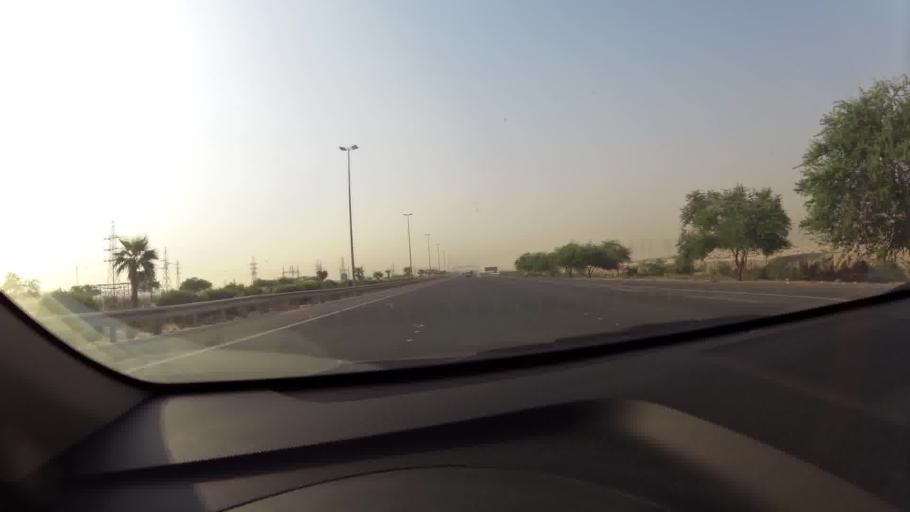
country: KW
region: Al Ahmadi
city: Al Fahahil
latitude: 28.8996
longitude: 48.2192
